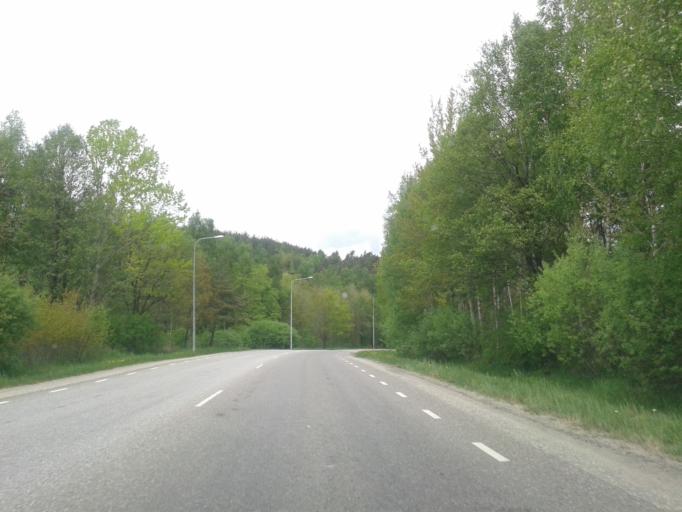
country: SE
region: Vaestra Goetaland
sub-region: Goteborg
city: Eriksbo
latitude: 57.7747
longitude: 12.0496
